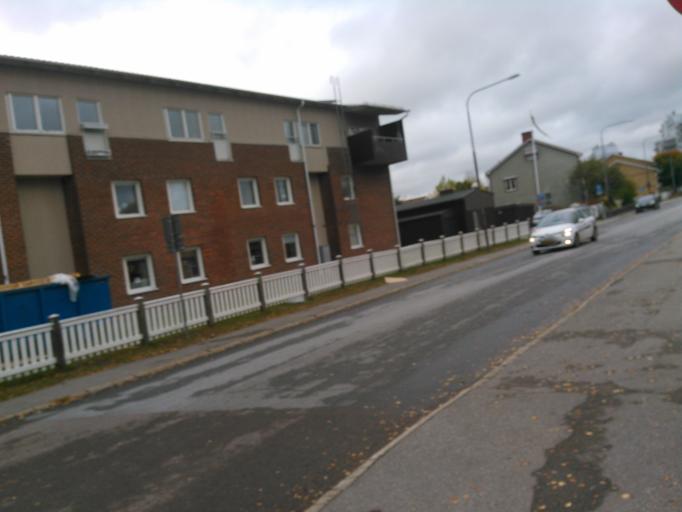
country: SE
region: Vaesterbotten
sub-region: Umea Kommun
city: Umea
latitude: 63.8208
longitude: 20.2475
